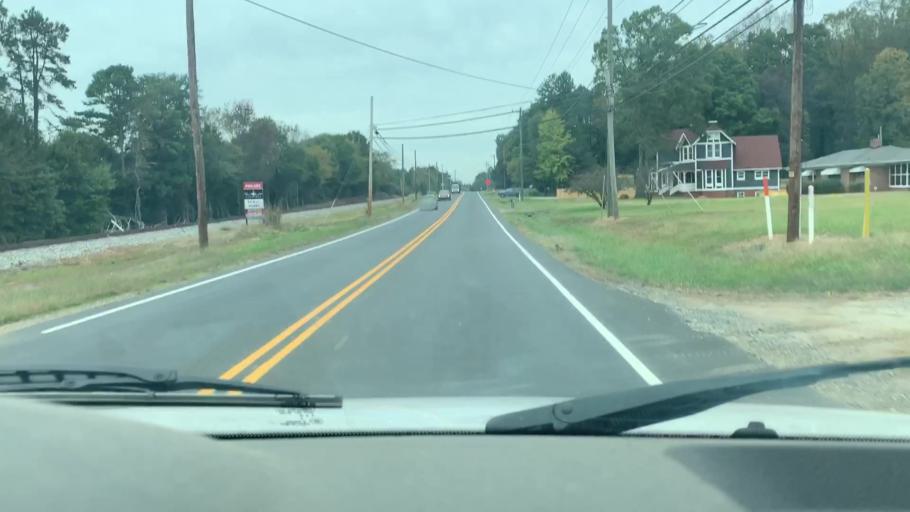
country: US
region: North Carolina
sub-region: Gaston County
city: Davidson
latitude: 35.5214
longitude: -80.8416
